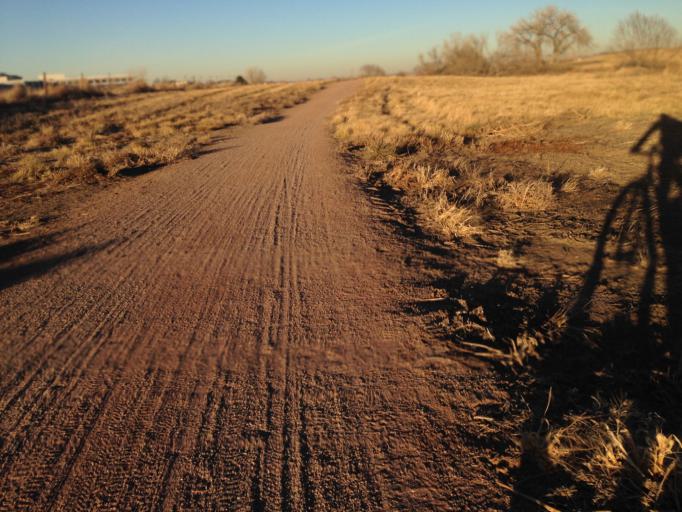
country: US
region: Colorado
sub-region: Boulder County
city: Lafayette
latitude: 39.9628
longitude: -105.0859
